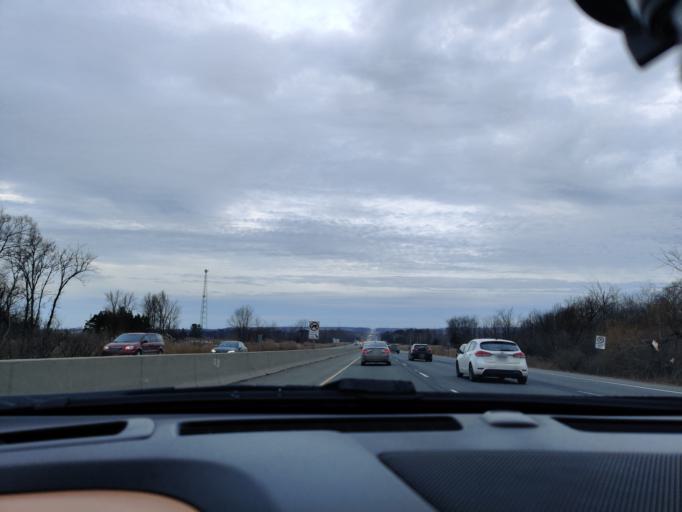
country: CA
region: Ontario
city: Cobourg
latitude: 43.9641
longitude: -78.3407
